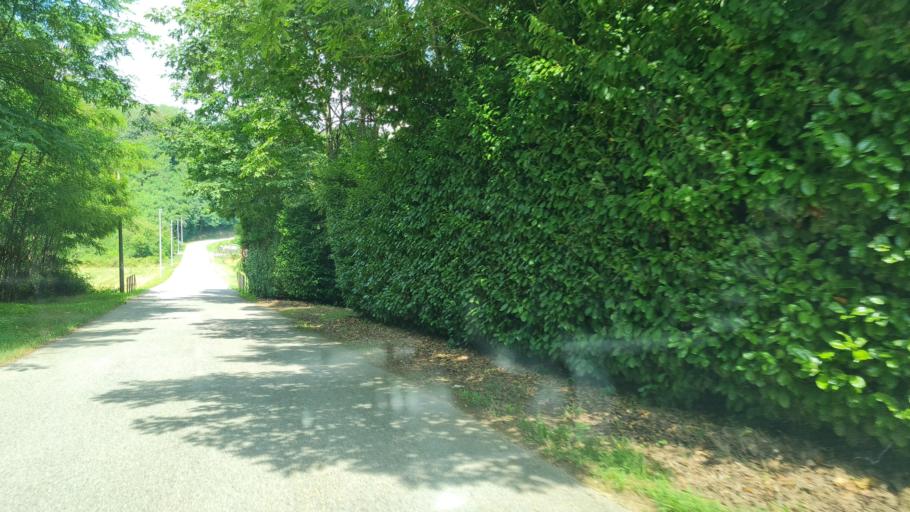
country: IT
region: Piedmont
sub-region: Provincia di Biella
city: Lessona
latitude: 45.5764
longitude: 8.2073
